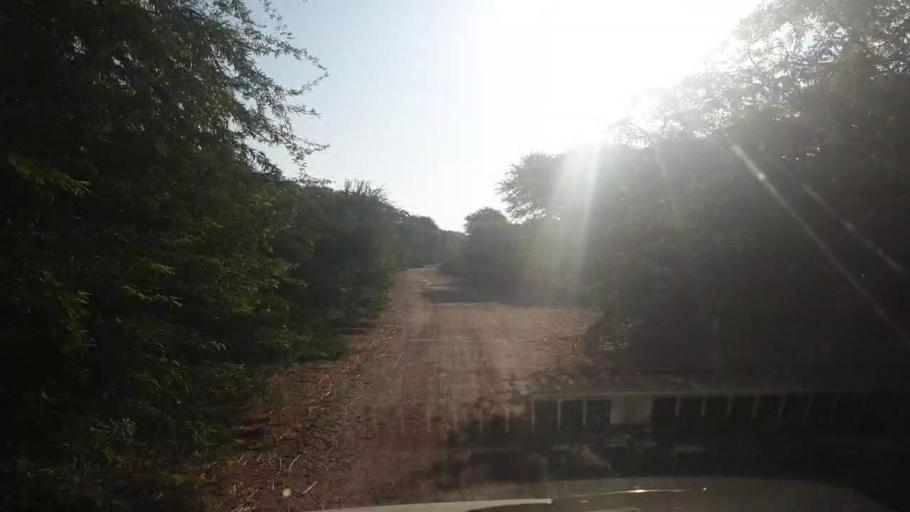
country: PK
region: Sindh
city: Talhar
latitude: 24.8078
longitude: 68.8472
